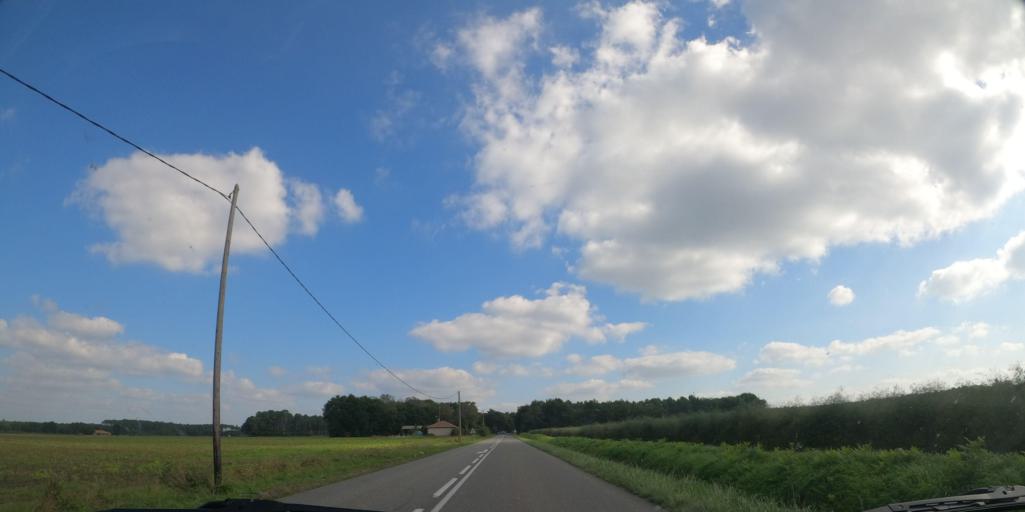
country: FR
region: Aquitaine
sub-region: Departement des Landes
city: Soustons
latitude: 43.7445
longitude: -1.3036
